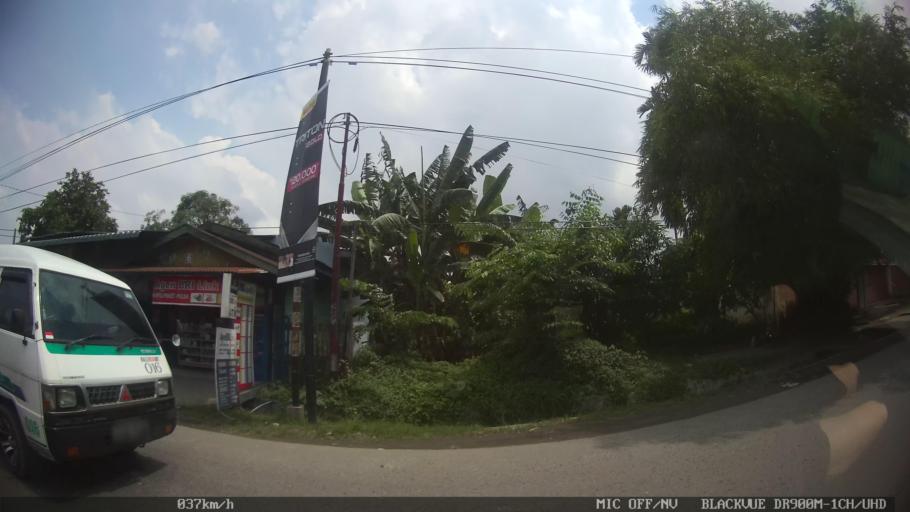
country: ID
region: North Sumatra
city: Medan
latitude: 3.6429
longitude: 98.6713
